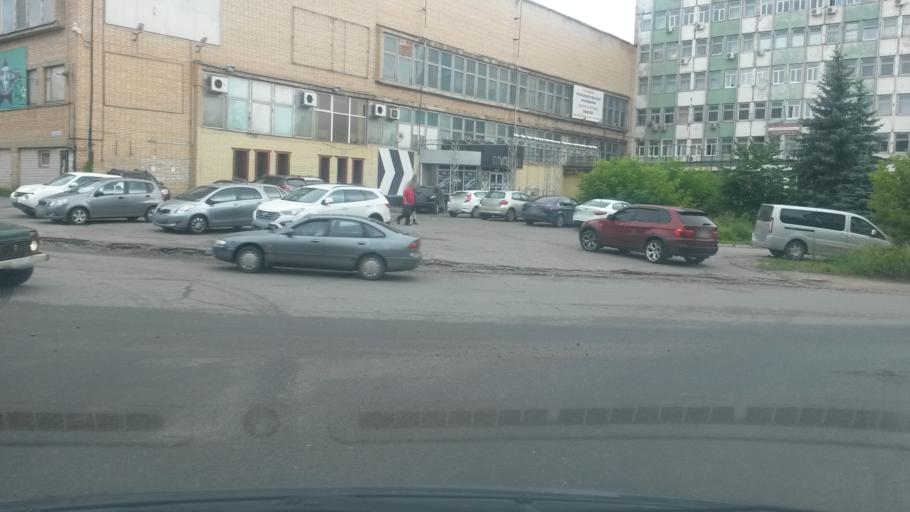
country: RU
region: Ivanovo
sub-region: Gorod Ivanovo
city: Ivanovo
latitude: 57.0087
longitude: 40.9575
